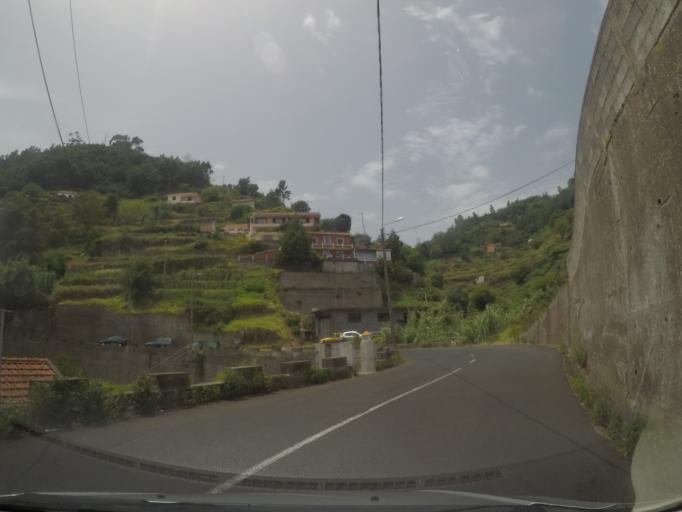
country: PT
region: Madeira
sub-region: Santa Cruz
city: Camacha
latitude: 32.6718
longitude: -16.8404
